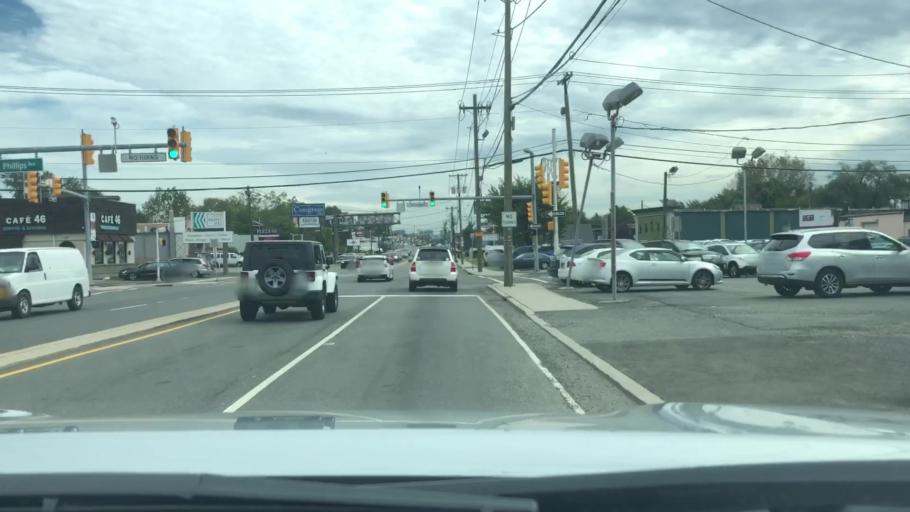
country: US
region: New Jersey
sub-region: Bergen County
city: Little Ferry
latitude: 40.8557
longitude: -74.0473
